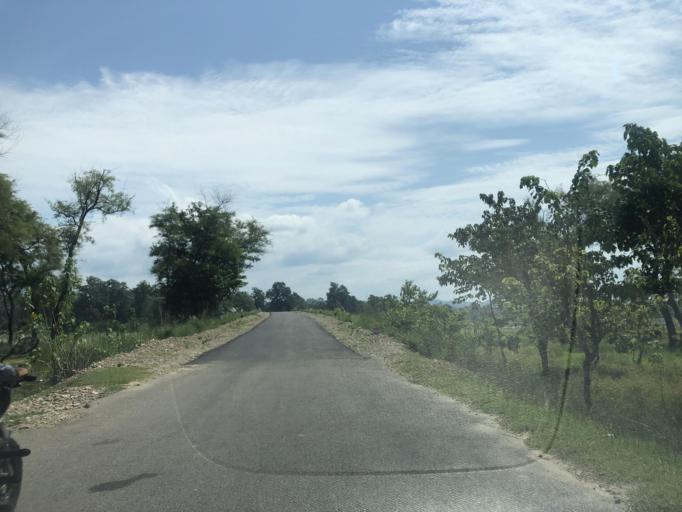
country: NP
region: Far Western
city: Tikapur
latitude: 28.5109
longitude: 81.3148
